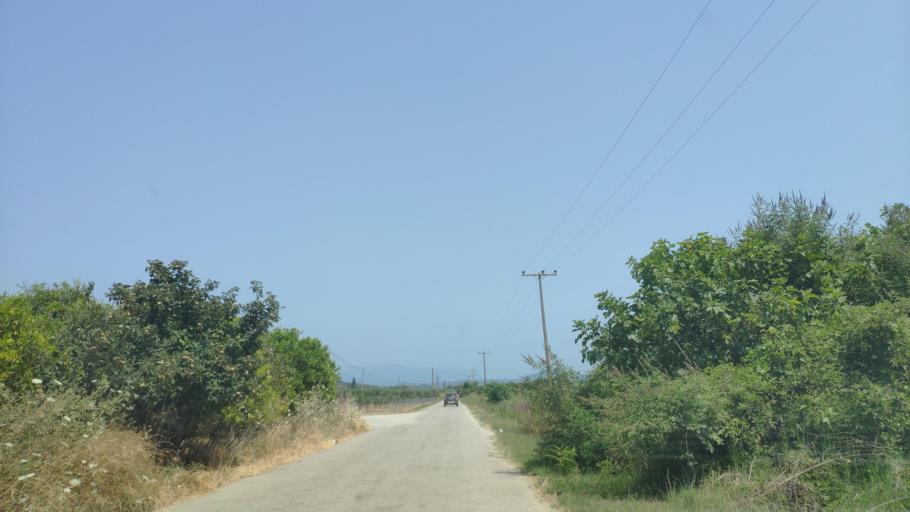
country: GR
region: Epirus
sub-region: Nomos Artas
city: Kompoti
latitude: 39.0569
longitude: 21.0689
